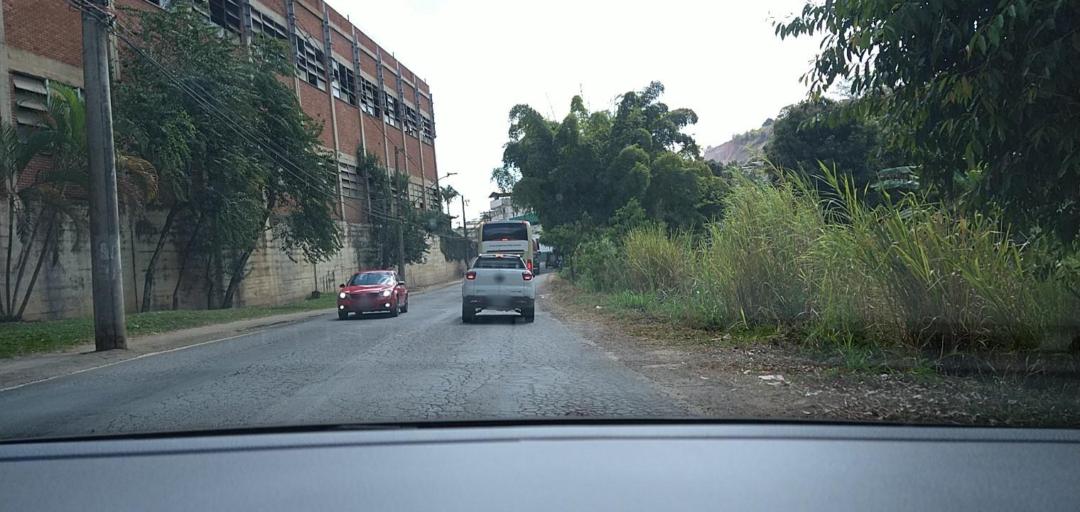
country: BR
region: Minas Gerais
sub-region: Ponte Nova
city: Ponte Nova
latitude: -20.4219
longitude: -42.8986
